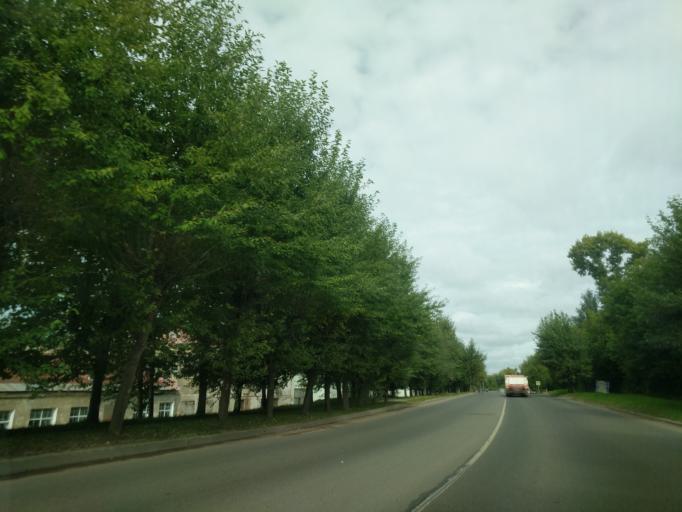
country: RU
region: Kirov
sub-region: Kirovo-Chepetskiy Rayon
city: Kirov
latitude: 58.6012
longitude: 49.6446
